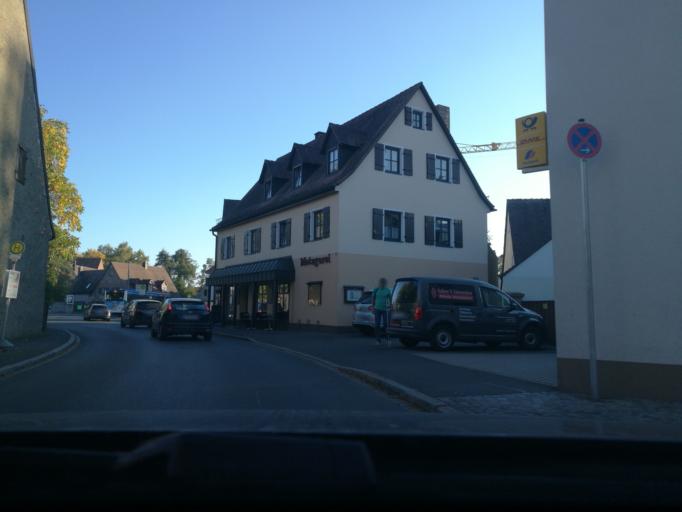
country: DE
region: Bavaria
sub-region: Regierungsbezirk Mittelfranken
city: Furth
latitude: 49.5276
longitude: 11.0107
